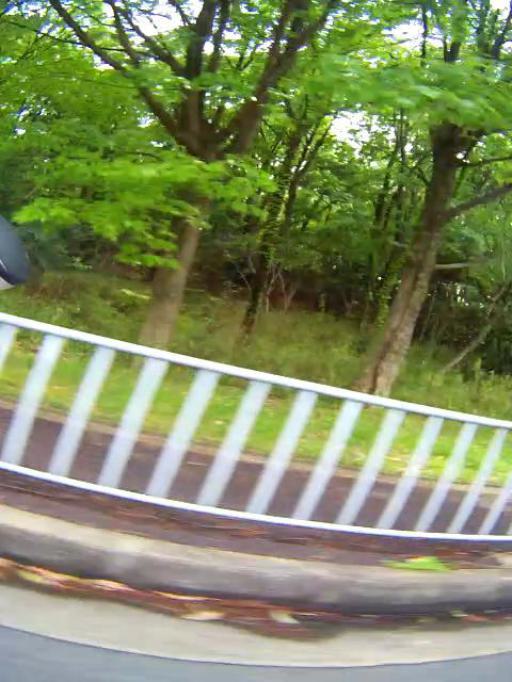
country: JP
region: Osaka
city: Toyonaka
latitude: 34.7805
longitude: 135.4901
